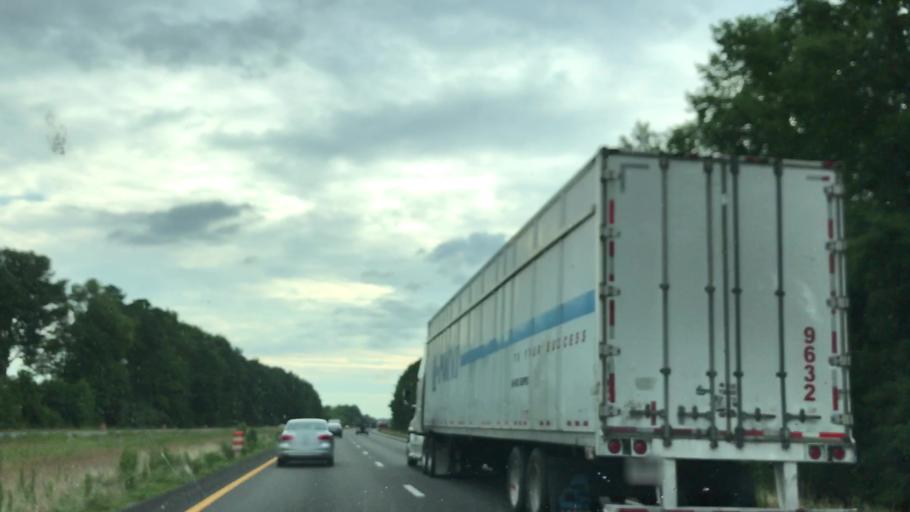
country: US
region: North Carolina
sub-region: Johnston County
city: Smithfield
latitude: 35.4725
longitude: -78.3745
